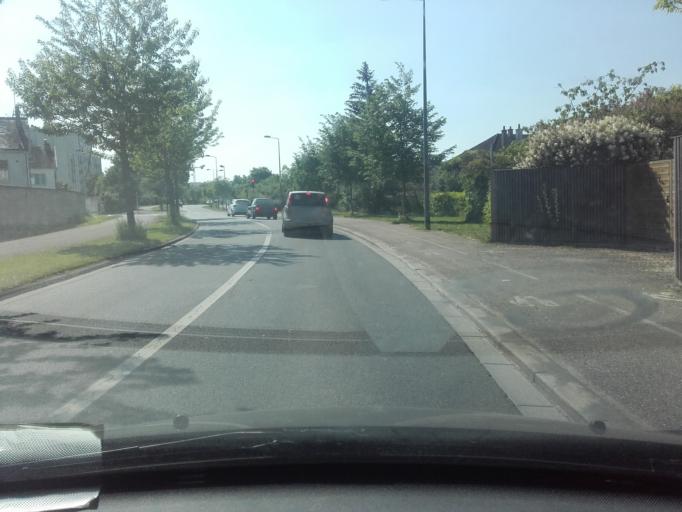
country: FR
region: Centre
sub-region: Departement d'Indre-et-Loire
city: Saint-Cyr-sur-Loire
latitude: 47.4189
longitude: 0.6823
